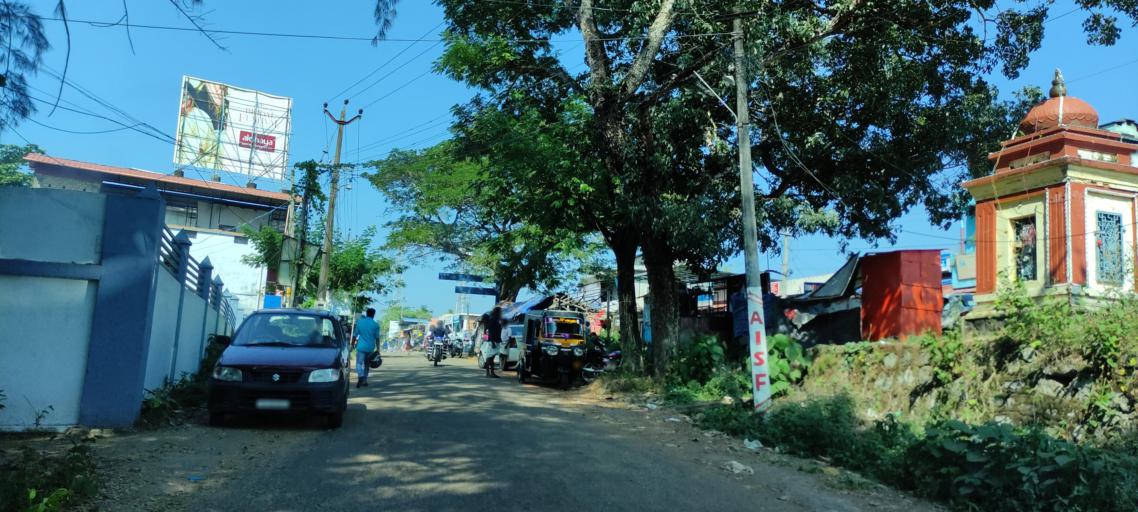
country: IN
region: Kerala
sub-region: Kollam
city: Panmana
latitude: 9.0423
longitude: 76.6279
